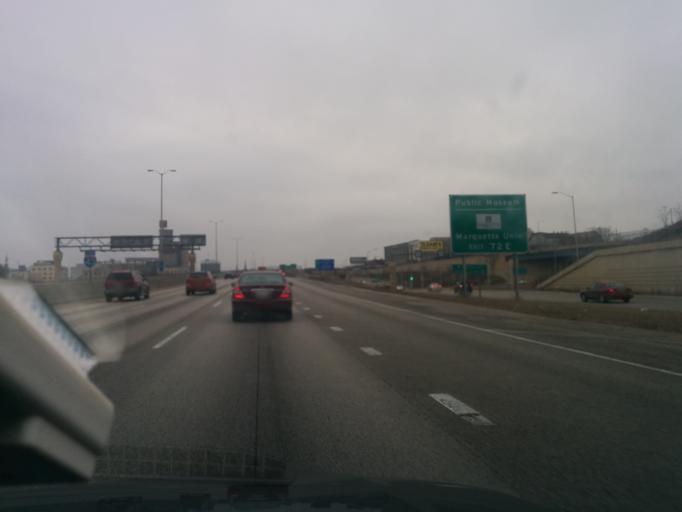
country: US
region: Wisconsin
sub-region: Milwaukee County
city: Milwaukee
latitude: 43.0523
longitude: -87.9255
